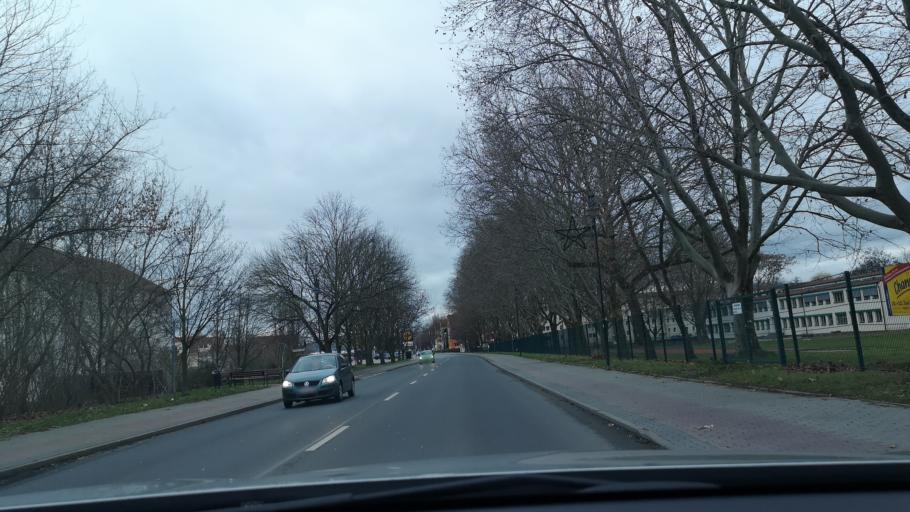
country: DE
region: Saxony-Anhalt
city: Braunsbedra
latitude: 51.2865
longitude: 11.8946
